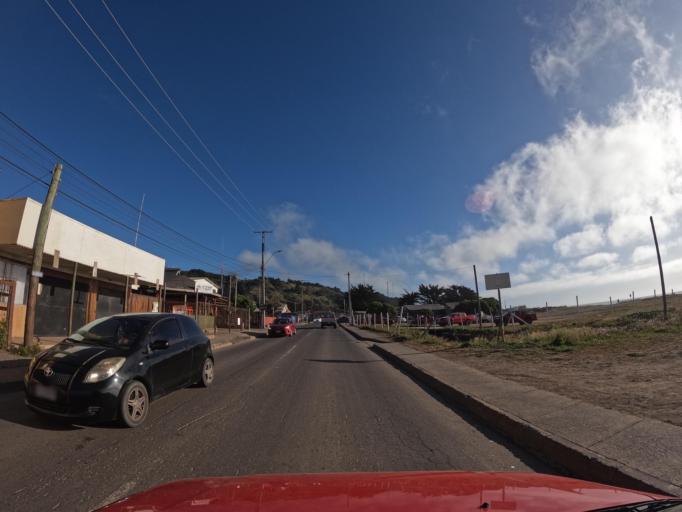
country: CL
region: Maule
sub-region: Provincia de Talca
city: Constitucion
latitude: -34.9336
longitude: -72.1806
